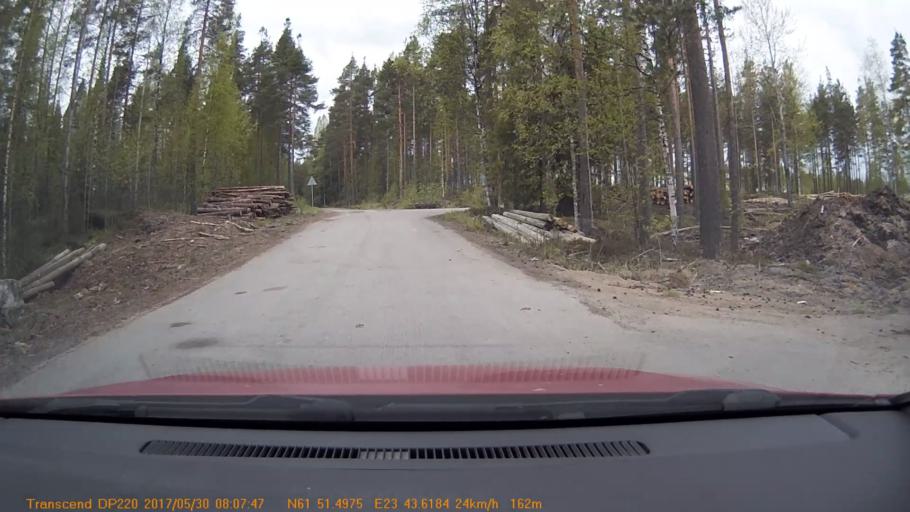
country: FI
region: Pirkanmaa
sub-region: Tampere
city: Kuru
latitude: 61.8583
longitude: 23.7272
